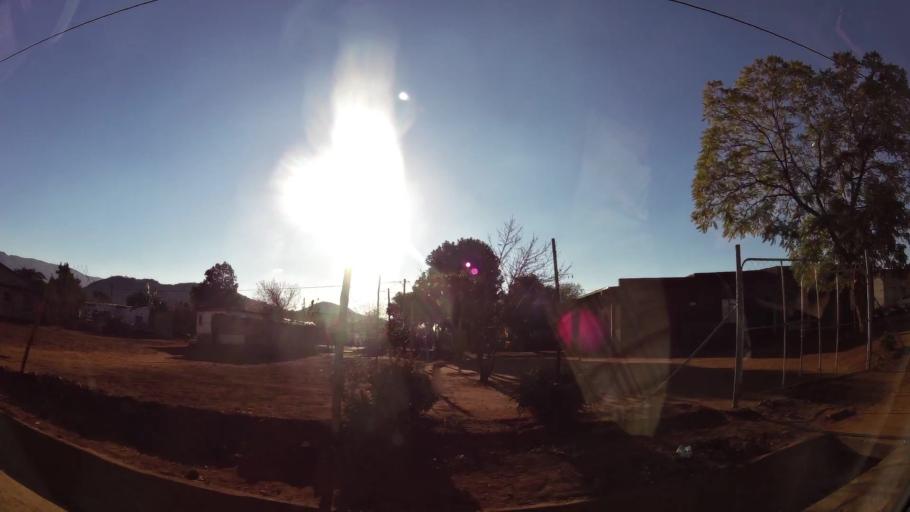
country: ZA
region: Limpopo
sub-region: Waterberg District Municipality
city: Mokopane
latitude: -24.1608
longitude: 28.9861
